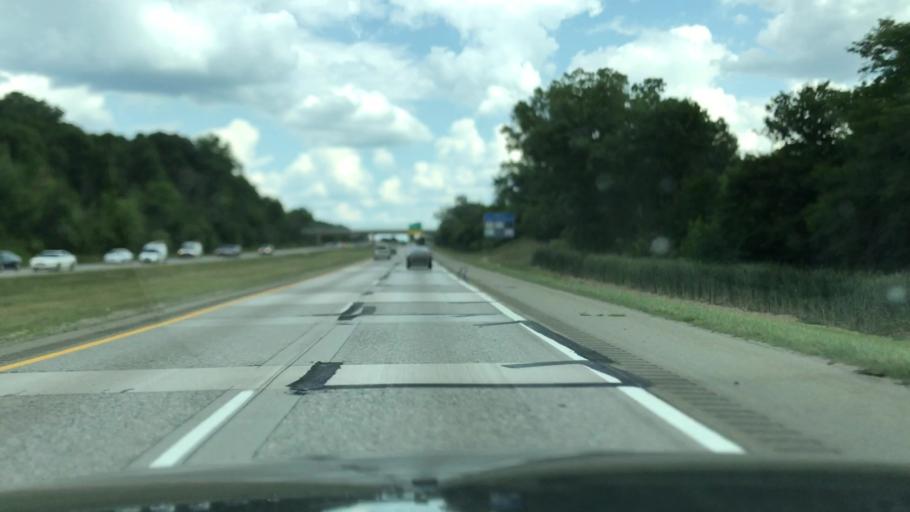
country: US
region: Michigan
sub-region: Kent County
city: East Grand Rapids
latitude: 42.9766
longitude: -85.6149
